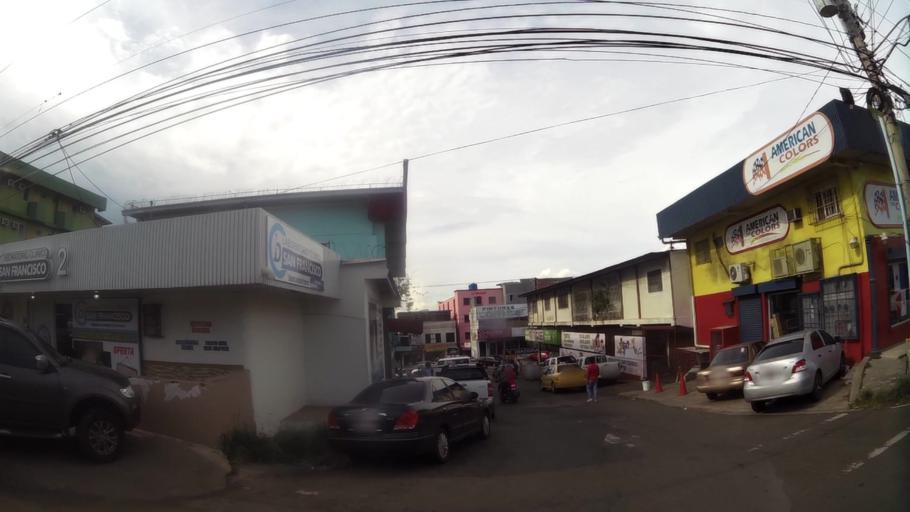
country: PA
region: Panama
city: La Chorrera
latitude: 8.8778
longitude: -79.7833
